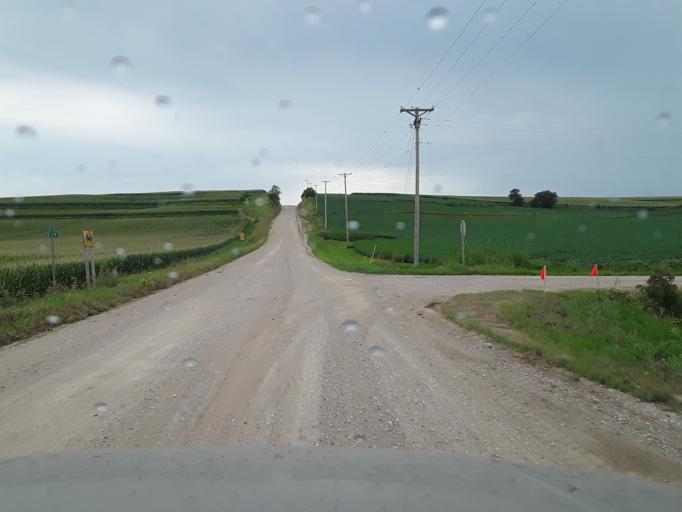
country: US
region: Nebraska
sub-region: Washington County
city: Blair
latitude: 41.5092
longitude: -96.1742
